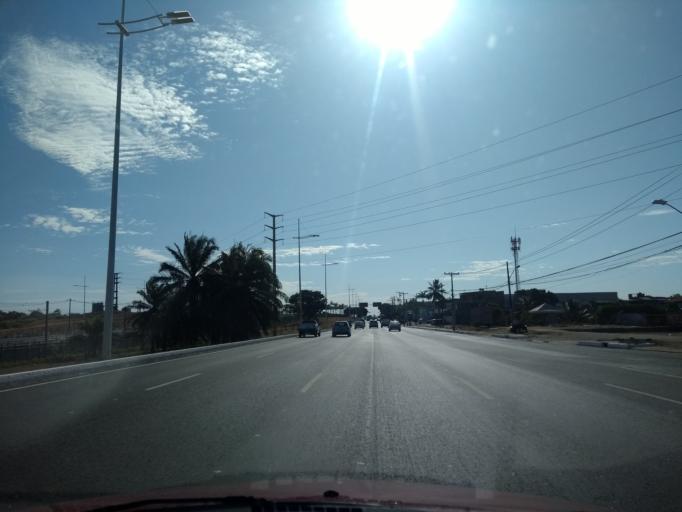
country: BR
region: Bahia
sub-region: Lauro De Freitas
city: Lauro de Freitas
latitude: -12.9219
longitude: -38.3630
